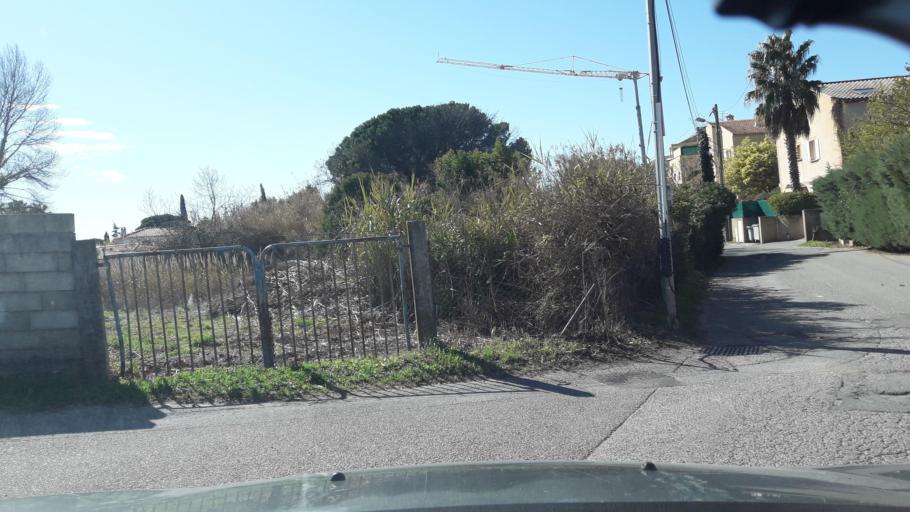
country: FR
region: Provence-Alpes-Cote d'Azur
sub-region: Departement du Var
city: Frejus
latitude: 43.4411
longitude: 6.7574
